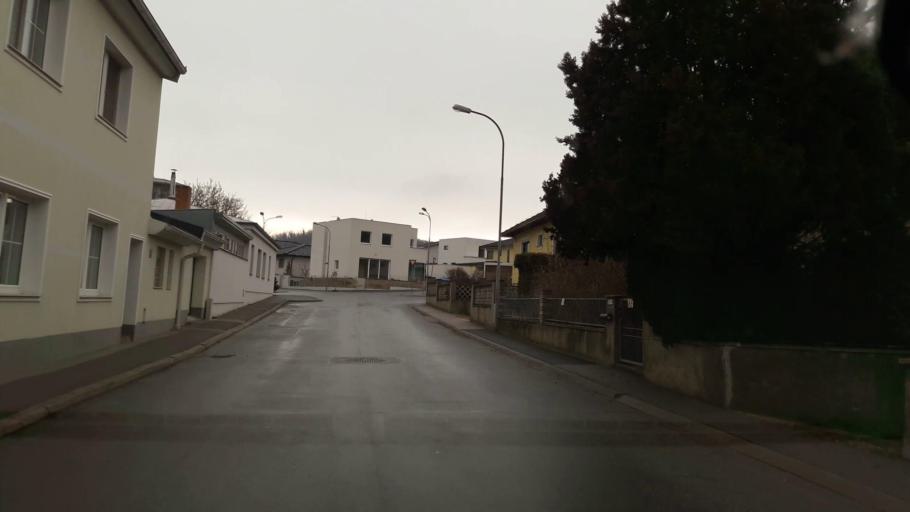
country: AT
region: Lower Austria
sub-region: Politischer Bezirk Bruck an der Leitha
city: Hainburg an der Donau
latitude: 48.1396
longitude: 16.9532
